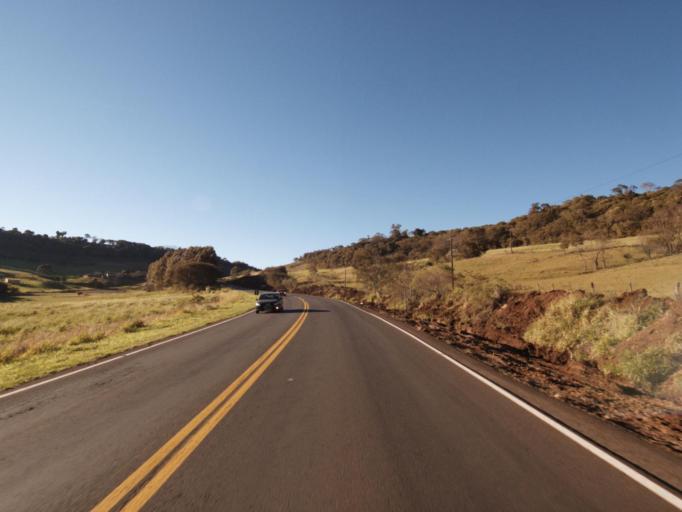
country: AR
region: Misiones
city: Bernardo de Irigoyen
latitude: -26.3554
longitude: -53.5426
